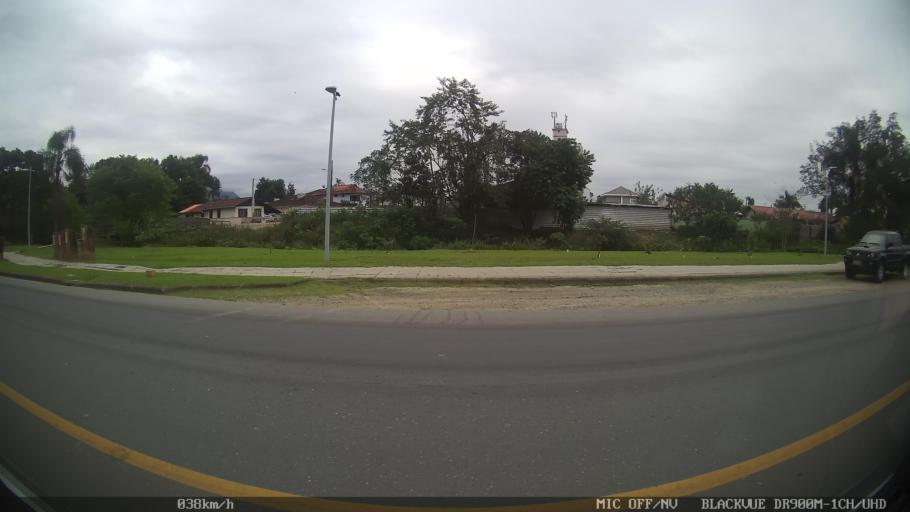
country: BR
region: Santa Catarina
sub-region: Joinville
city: Joinville
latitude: -26.2682
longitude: -48.8641
